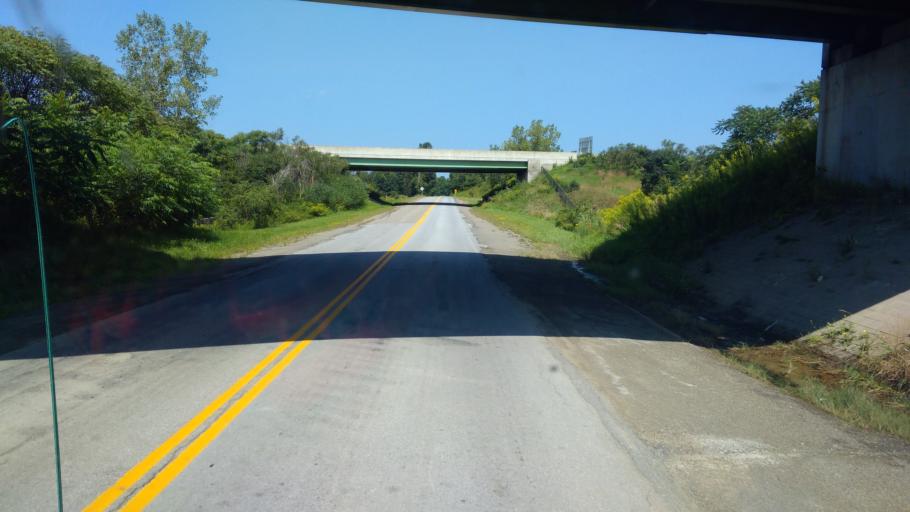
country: US
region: New York
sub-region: Allegany County
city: Belmont
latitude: 42.2701
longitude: -78.0509
